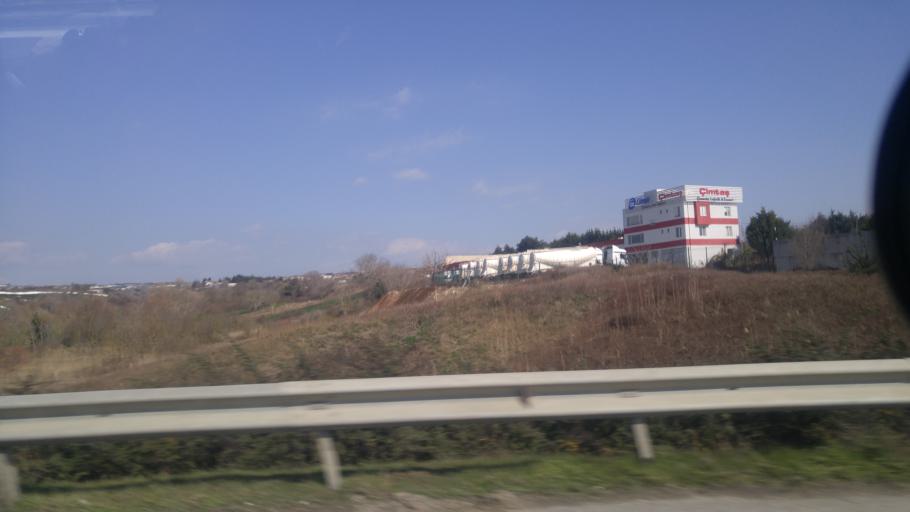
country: TR
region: Istanbul
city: Ortakoy
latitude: 41.0913
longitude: 28.3633
